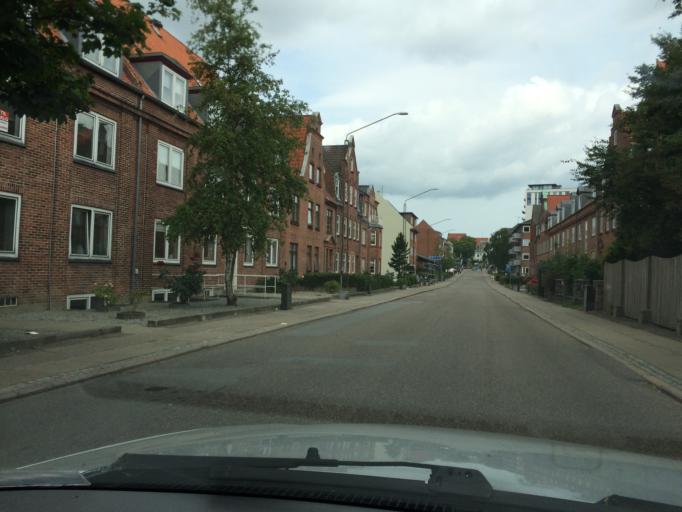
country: DK
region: South Denmark
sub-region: Sonderborg Kommune
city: Sonderborg
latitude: 54.9068
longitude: 9.7901
